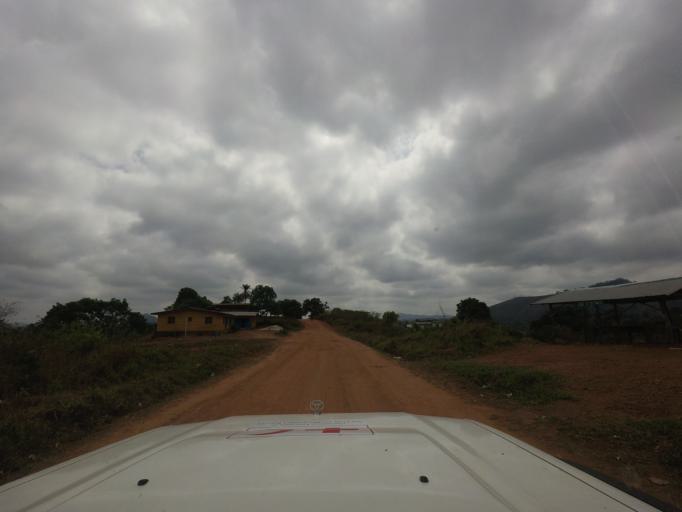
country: LR
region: Lofa
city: Voinjama
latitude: 8.4162
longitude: -9.7439
